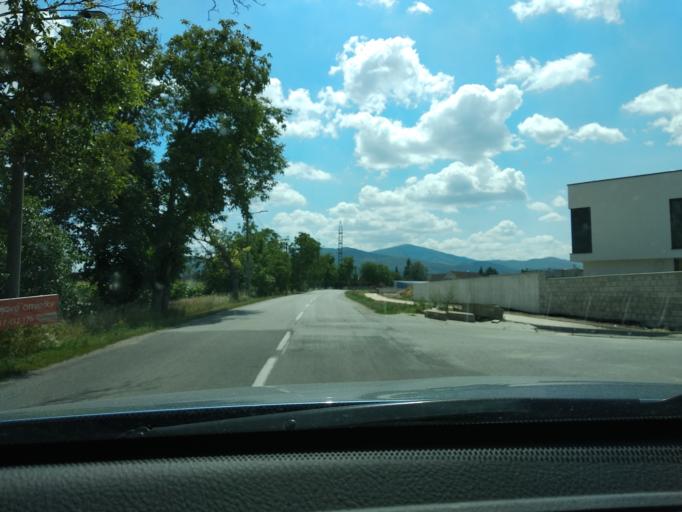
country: SK
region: Trenciansky
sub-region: Okres Trencin
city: Trencin
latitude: 48.8562
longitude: 18.0180
